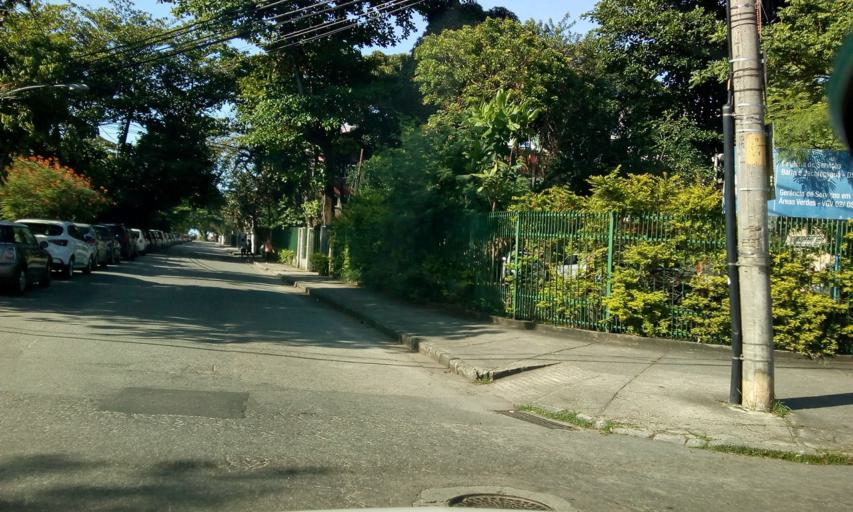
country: BR
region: Rio de Janeiro
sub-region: Rio De Janeiro
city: Rio de Janeiro
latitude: -23.0093
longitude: -43.3125
